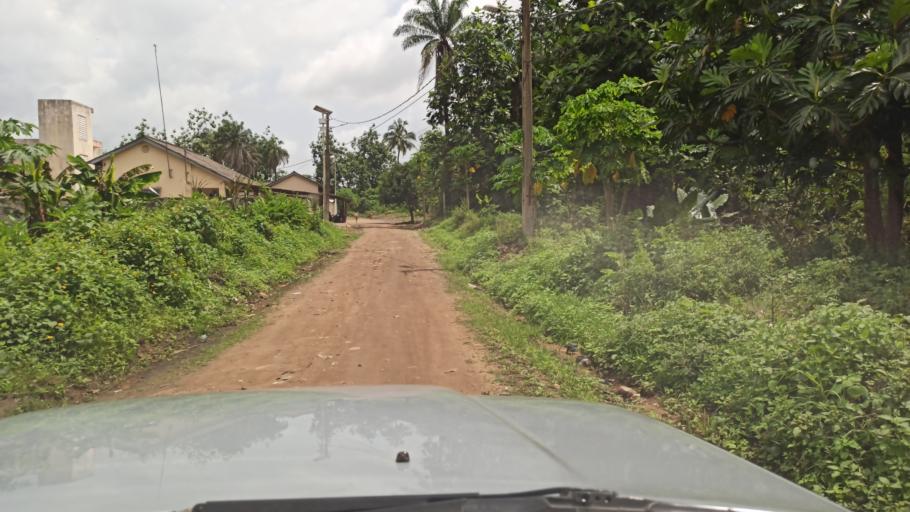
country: BJ
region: Queme
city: Porto-Novo
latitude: 6.4669
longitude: 2.6331
